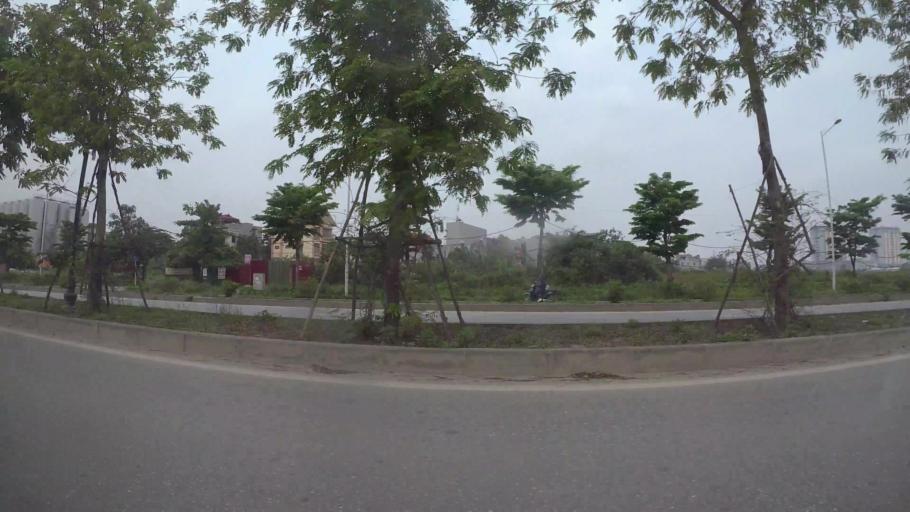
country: VN
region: Ha Noi
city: Cau Dien
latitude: 21.0385
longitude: 105.7446
